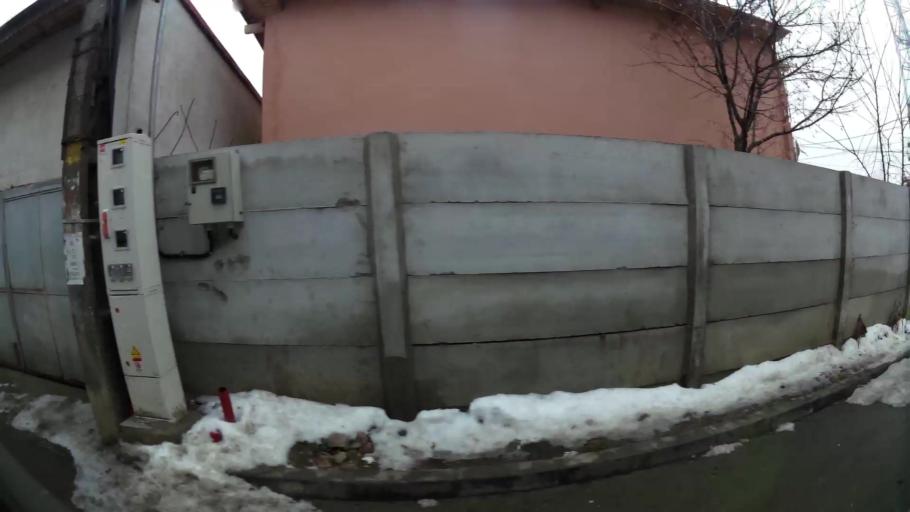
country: RO
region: Ilfov
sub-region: Comuna Chiajna
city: Rosu
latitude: 44.4478
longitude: 26.0104
